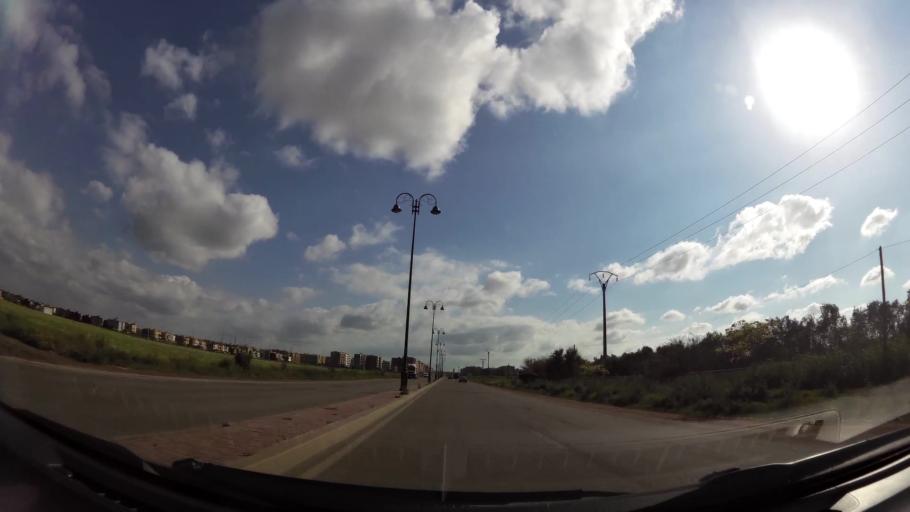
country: MA
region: Chaouia-Ouardigha
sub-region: Settat Province
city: Berrechid
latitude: 33.2836
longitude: -7.5786
